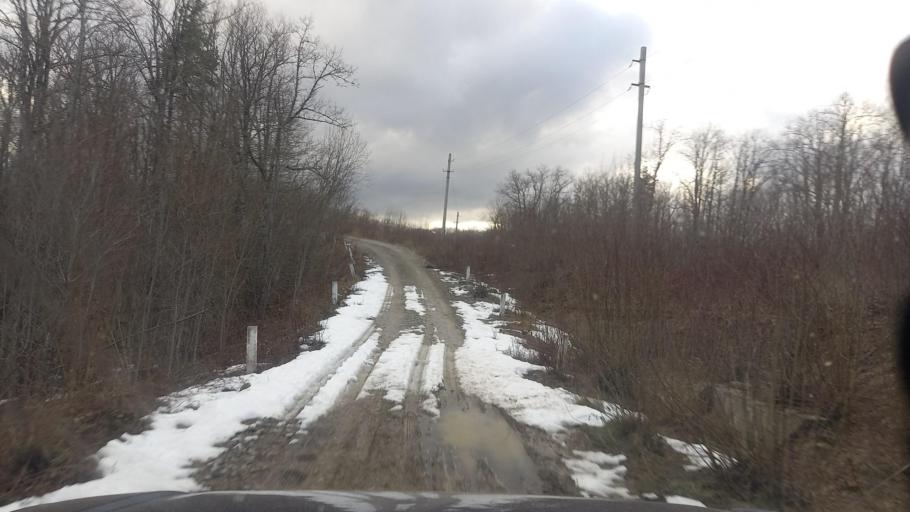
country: RU
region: Krasnodarskiy
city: Smolenskaya
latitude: 44.5733
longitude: 38.7997
